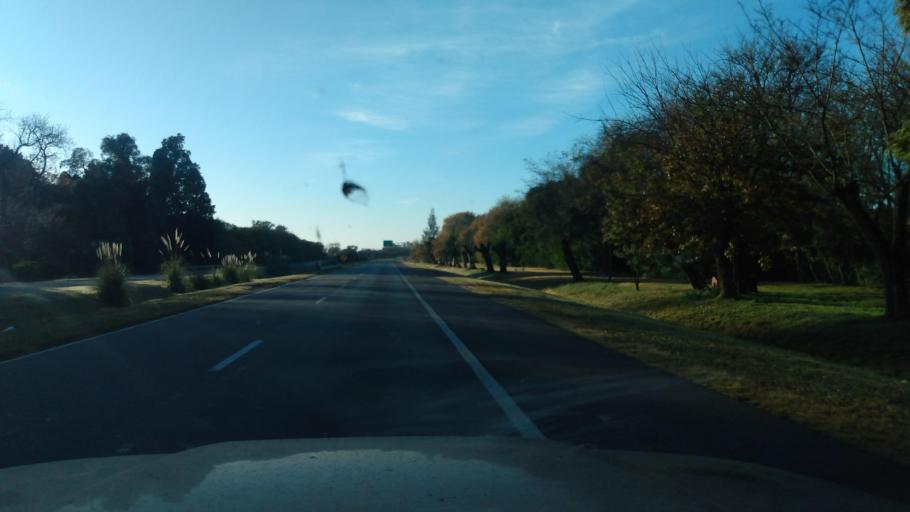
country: AR
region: Buenos Aires
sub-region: Partido de Lujan
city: Lujan
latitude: -34.5470
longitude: -59.2054
